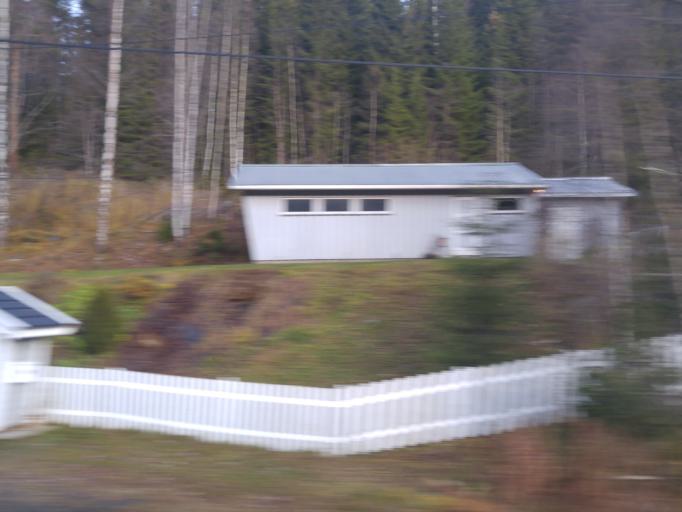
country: NO
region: Oppland
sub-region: Nord-Aurdal
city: Fagernes
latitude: 61.0369
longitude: 9.1761
